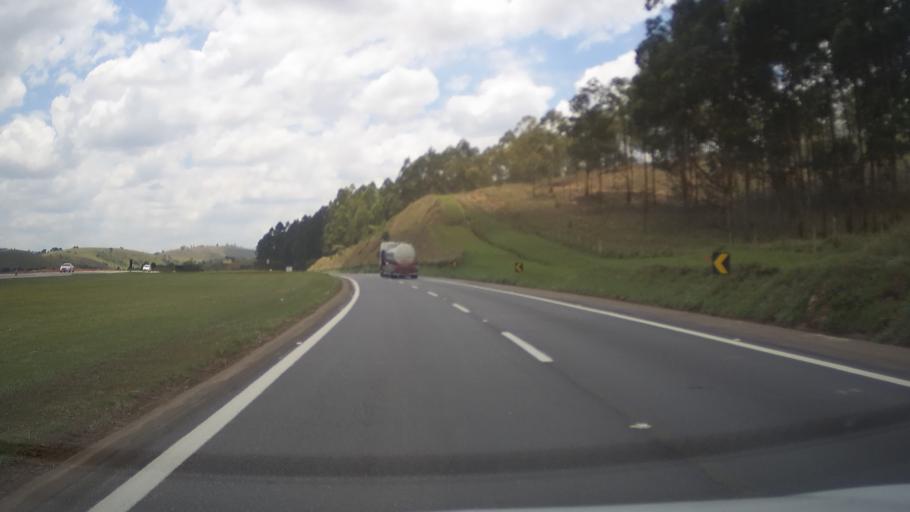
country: BR
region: Minas Gerais
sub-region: Campanha
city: Campanha
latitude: -21.7233
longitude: -45.3806
